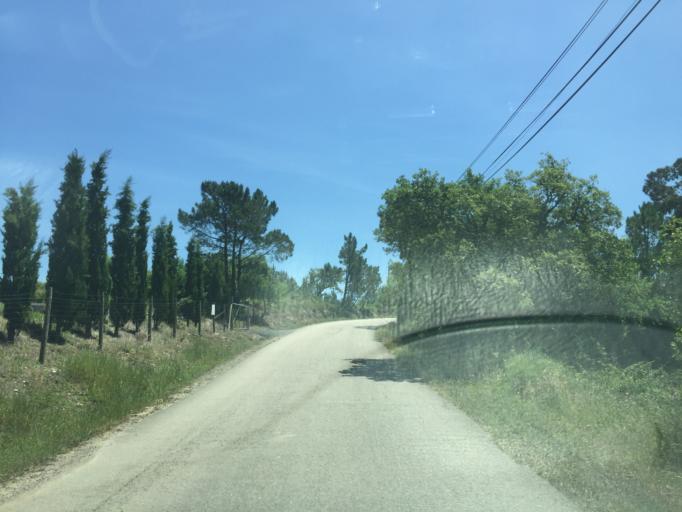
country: PT
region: Lisbon
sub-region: Mafra
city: Venda do Pinheiro
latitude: 38.8925
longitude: -9.2281
